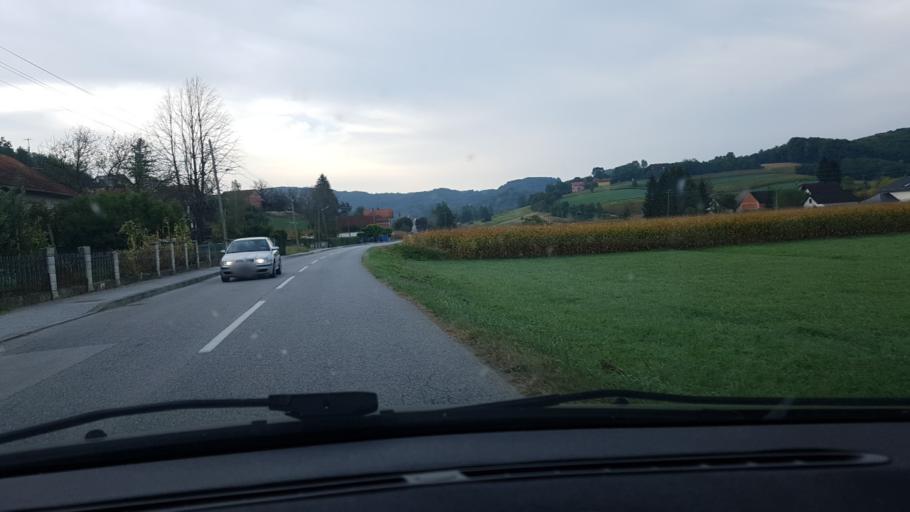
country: HR
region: Krapinsko-Zagorska
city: Mihovljan
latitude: 46.1395
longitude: 15.9644
